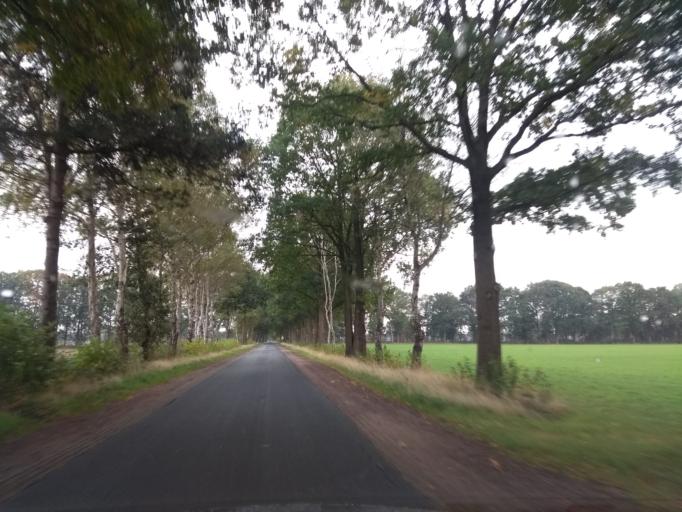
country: NL
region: Gelderland
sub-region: Gemeente Bronckhorst
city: Zelhem
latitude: 52.0216
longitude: 6.3679
